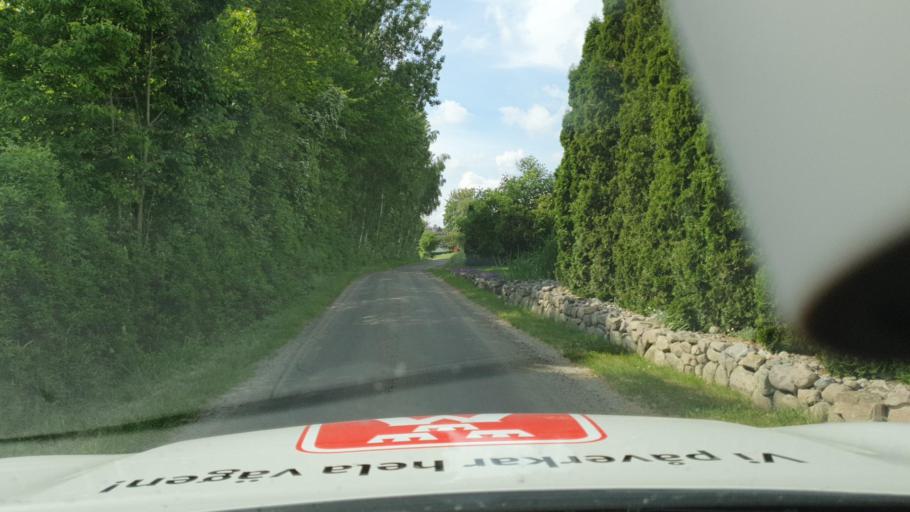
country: SE
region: Skane
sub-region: Skurups Kommun
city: Skurup
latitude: 55.5352
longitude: 13.5370
